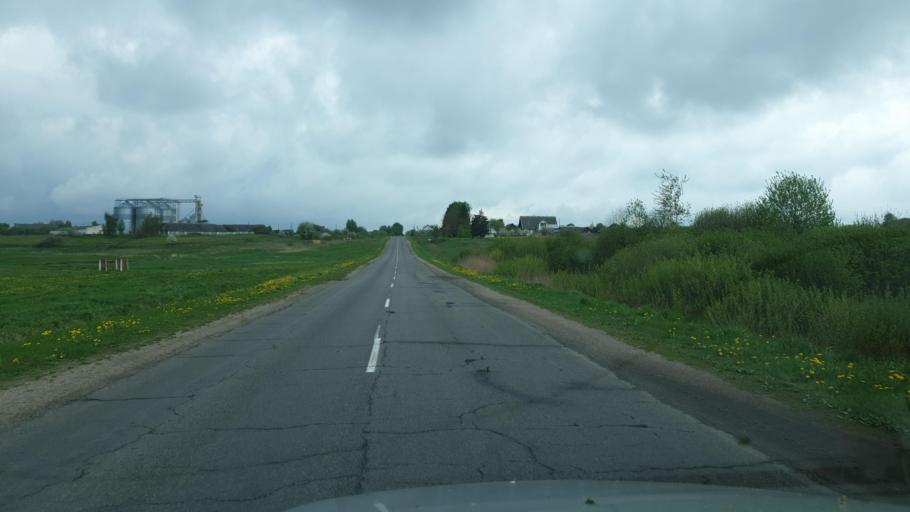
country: BY
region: Vitebsk
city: Lyepyel'
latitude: 54.8853
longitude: 28.6376
